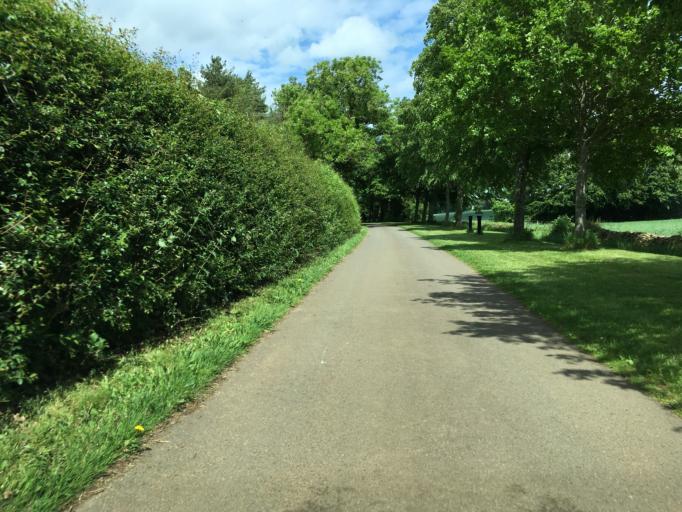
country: GB
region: England
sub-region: Gloucestershire
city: Tetbury
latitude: 51.6712
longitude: -2.1050
